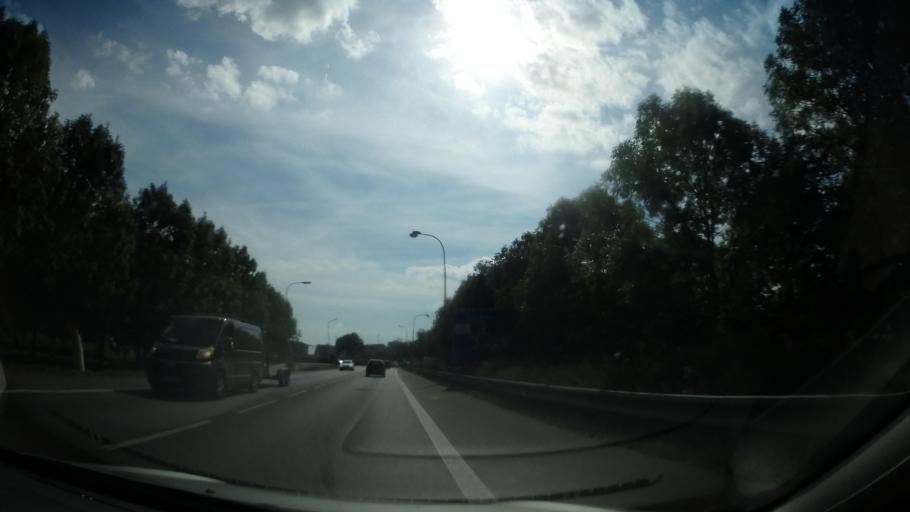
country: CZ
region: Jihocesky
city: Strakonice
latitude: 49.2615
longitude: 13.9146
